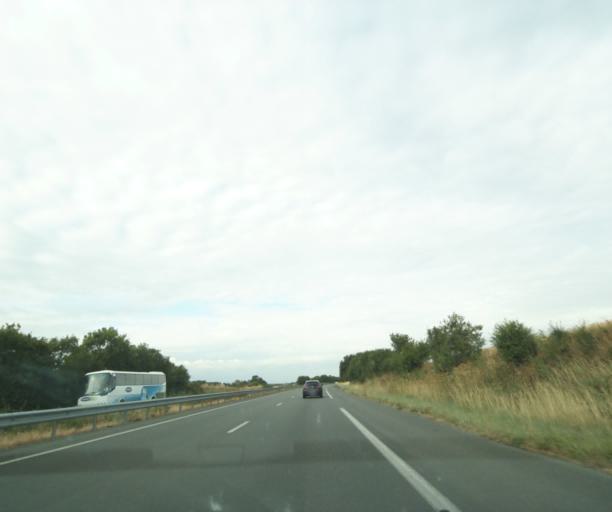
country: FR
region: Poitou-Charentes
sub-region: Departement de la Charente-Maritime
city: Dompierre-sur-Mer
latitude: 46.1925
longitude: -1.0672
